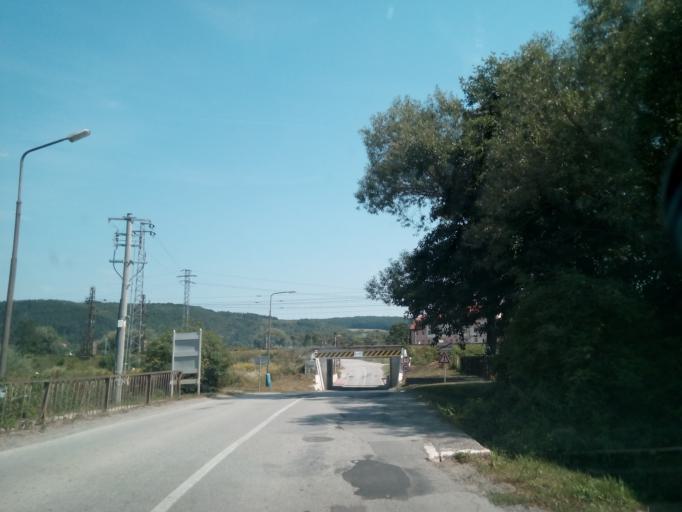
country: SK
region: Kosicky
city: Kosice
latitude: 48.7988
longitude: 21.2424
